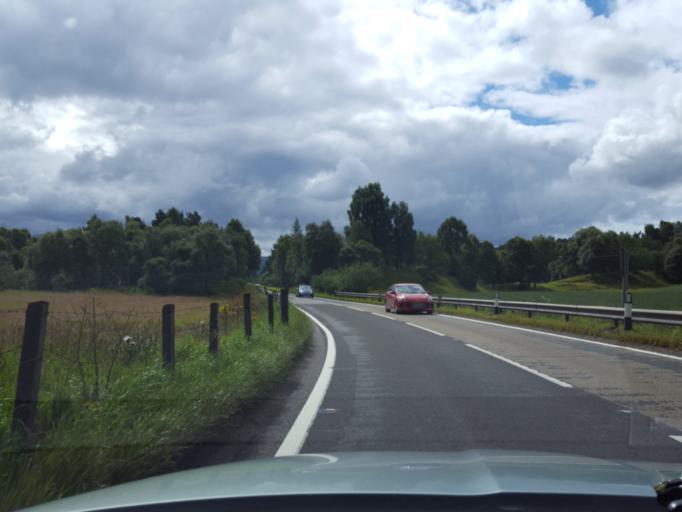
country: GB
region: Scotland
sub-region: Highland
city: Aviemore
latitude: 57.2269
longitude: -3.8159
